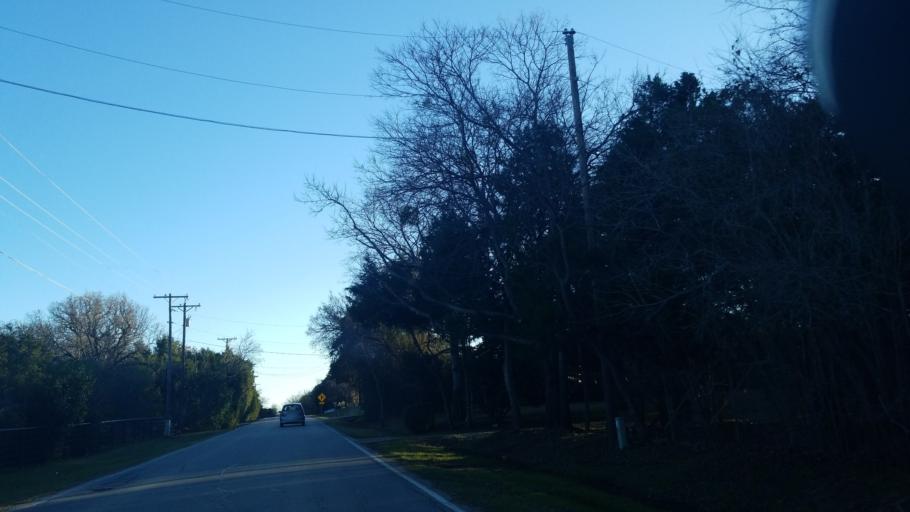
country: US
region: Texas
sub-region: Denton County
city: Shady Shores
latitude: 33.1459
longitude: -97.0299
